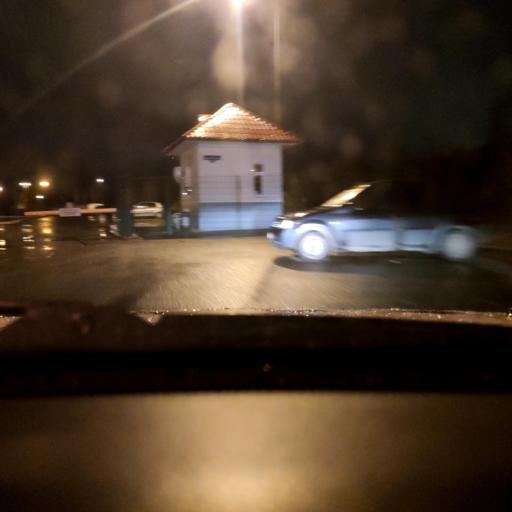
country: RU
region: Perm
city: Perm
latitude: 58.0348
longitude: 56.1771
